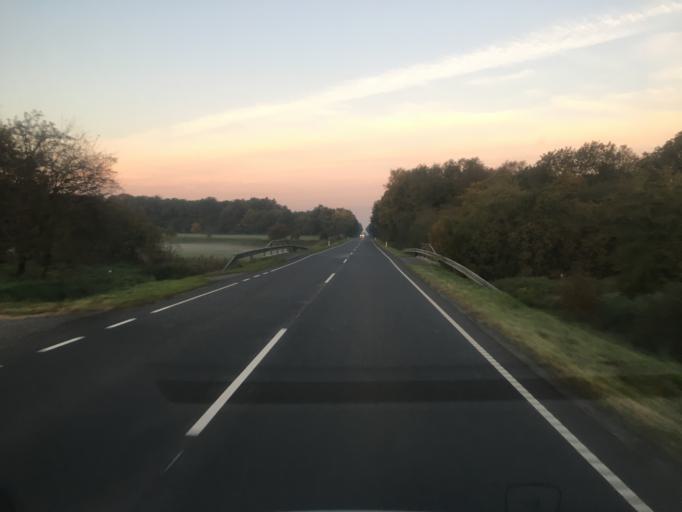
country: DK
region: South Denmark
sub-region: Aabenraa Kommune
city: Tinglev
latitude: 54.9740
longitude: 9.1282
